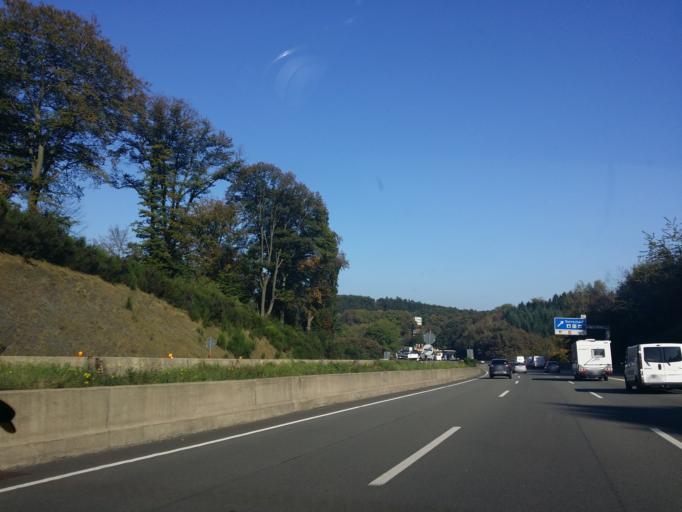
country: DE
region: North Rhine-Westphalia
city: Wermelskirchen
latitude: 51.1554
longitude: 7.2226
